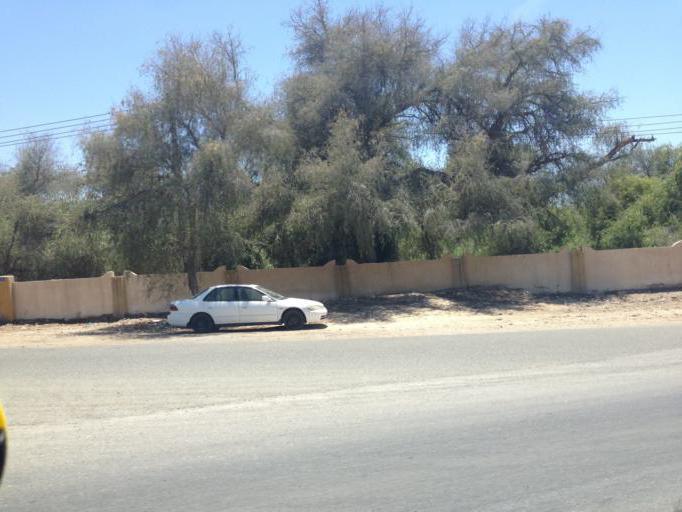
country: OM
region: Muhafazat Masqat
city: As Sib al Jadidah
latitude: 23.6637
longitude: 58.2052
